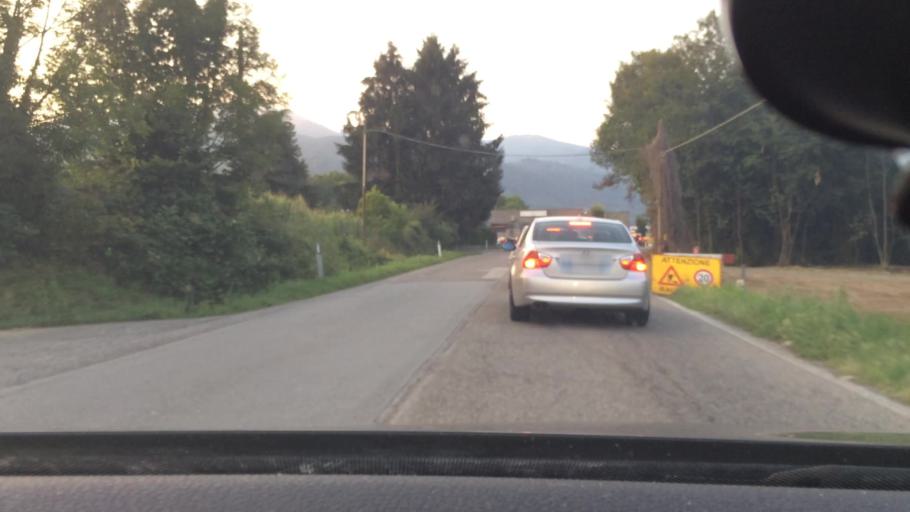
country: IT
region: Lombardy
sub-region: Provincia di Como
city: Alserio
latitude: 45.7865
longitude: 9.1961
